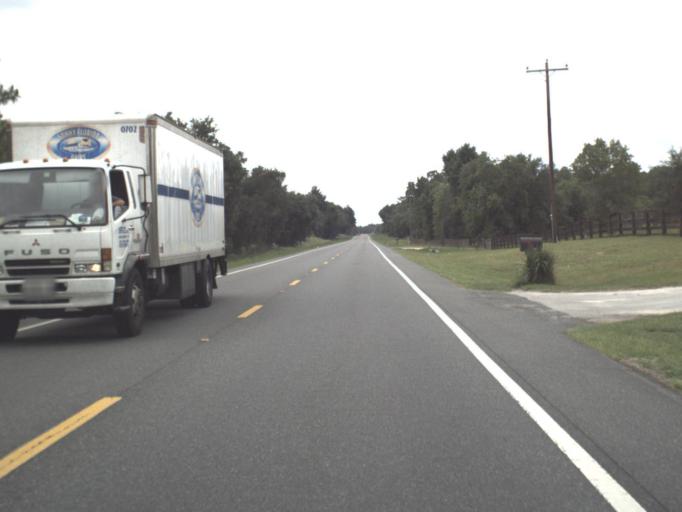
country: US
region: Florida
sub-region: Levy County
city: Williston Highlands
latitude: 29.2344
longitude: -82.4412
